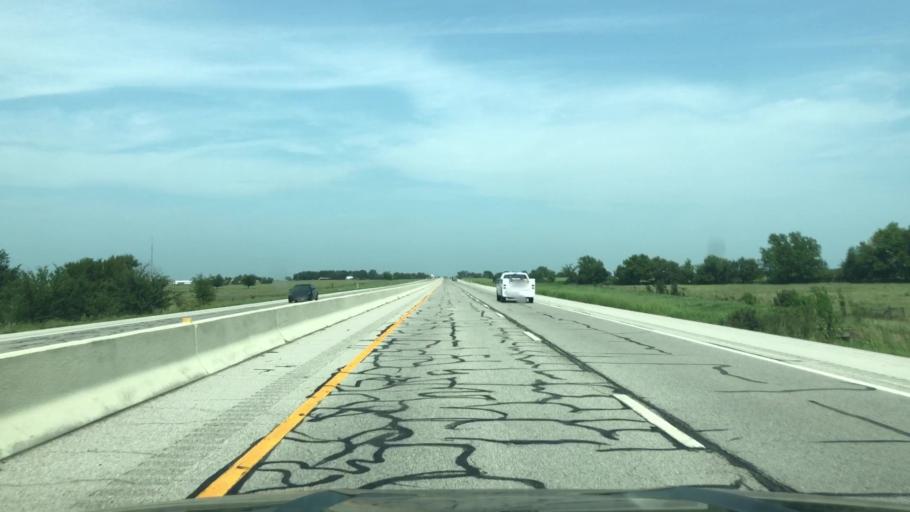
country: US
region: Oklahoma
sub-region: Craig County
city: Vinita
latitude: 36.5288
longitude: -95.2496
